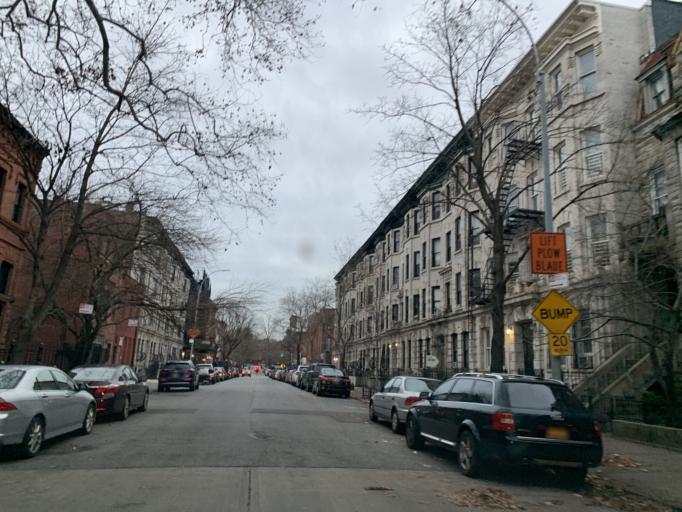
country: US
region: New York
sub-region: Kings County
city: Brooklyn
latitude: 40.6841
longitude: -73.9640
